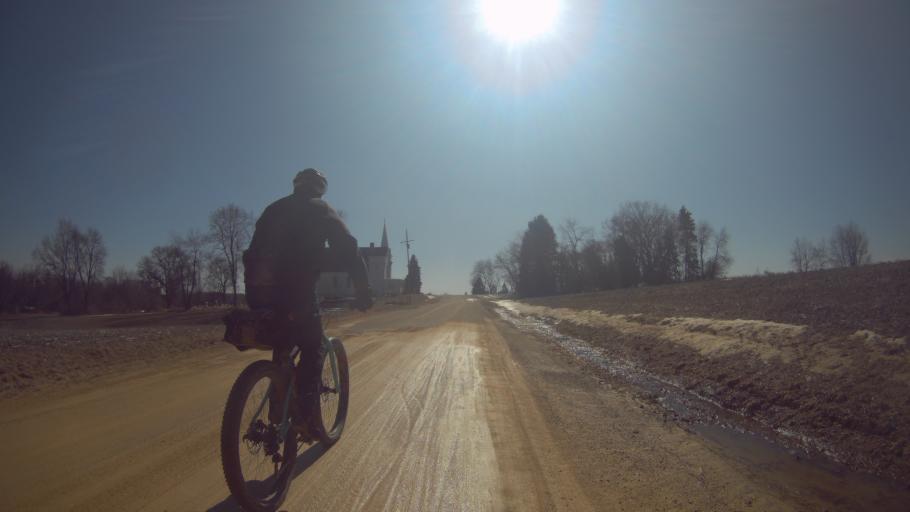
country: US
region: Illinois
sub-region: Winnebago County
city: Lake Summerset
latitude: 42.3810
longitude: -89.4081
